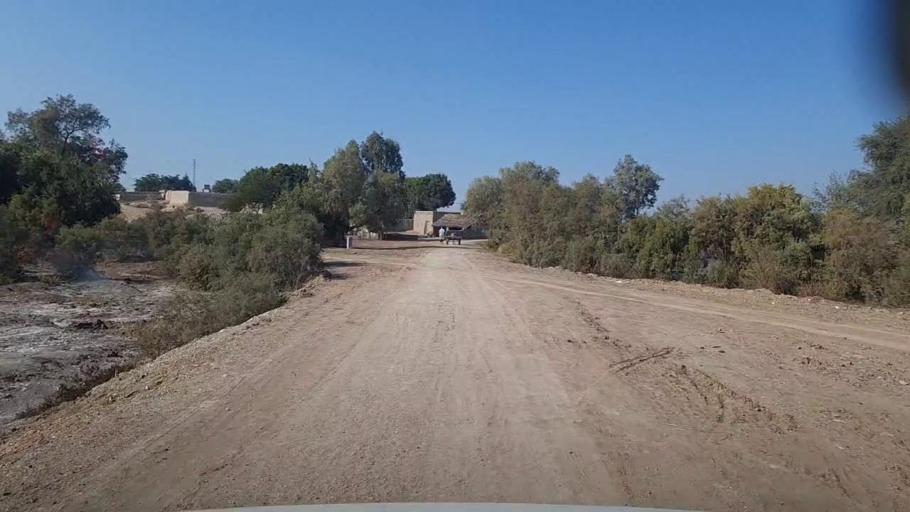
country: PK
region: Sindh
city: Khairpur
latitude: 27.9547
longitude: 69.7342
